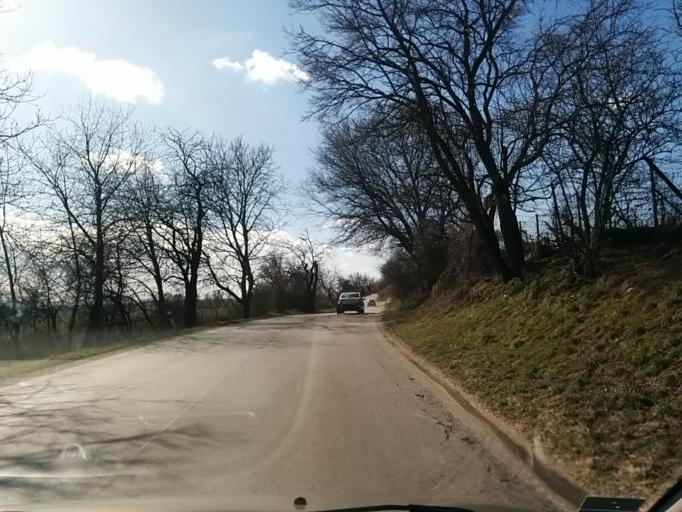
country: SK
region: Trenciansky
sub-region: Okres Nove Mesto nad Vahom
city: Nove Mesto nad Vahom
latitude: 48.7364
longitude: 17.8148
